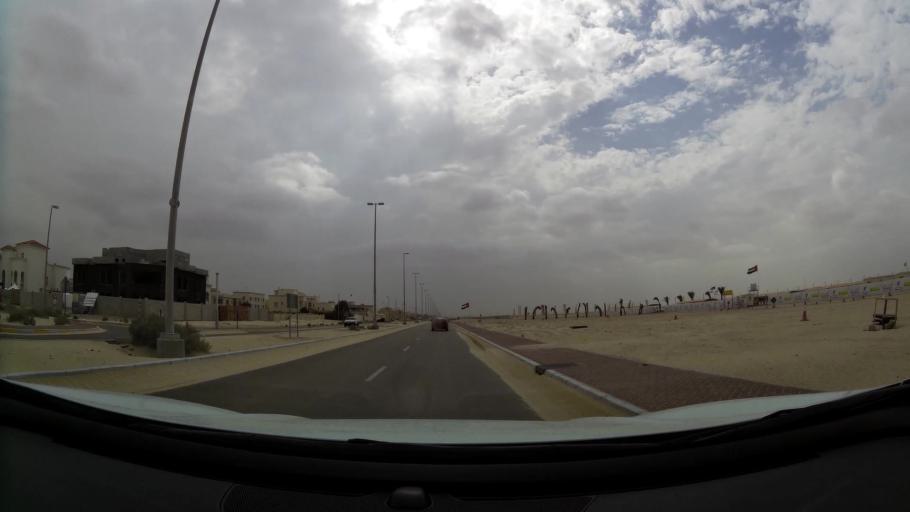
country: AE
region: Abu Dhabi
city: Abu Dhabi
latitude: 24.3954
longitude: 54.6457
